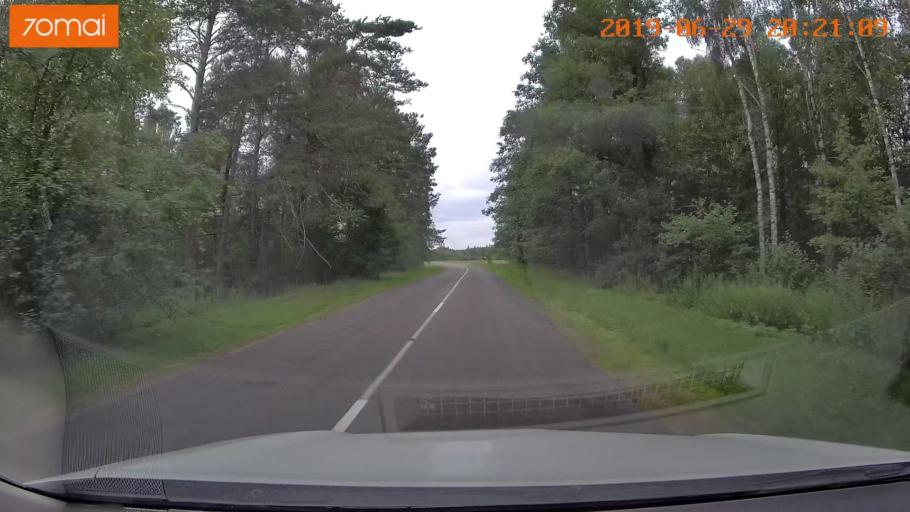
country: BY
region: Brest
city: Asnyezhytsy
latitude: 52.4168
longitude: 26.2522
